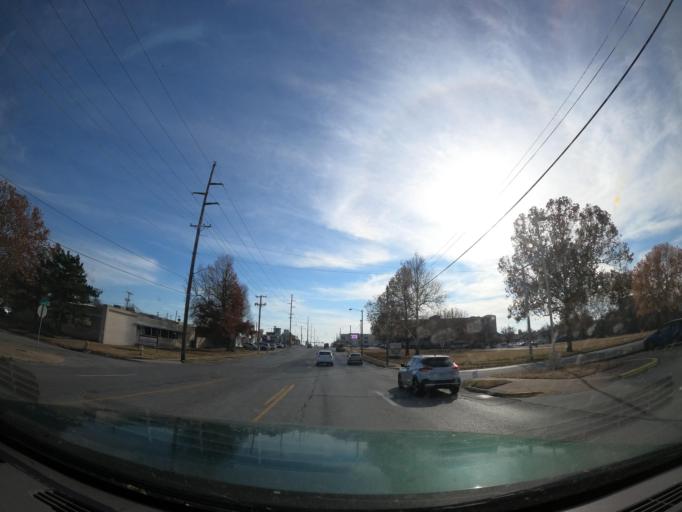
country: US
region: Oklahoma
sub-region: Tulsa County
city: Tulsa
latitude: 36.1217
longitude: -95.9403
